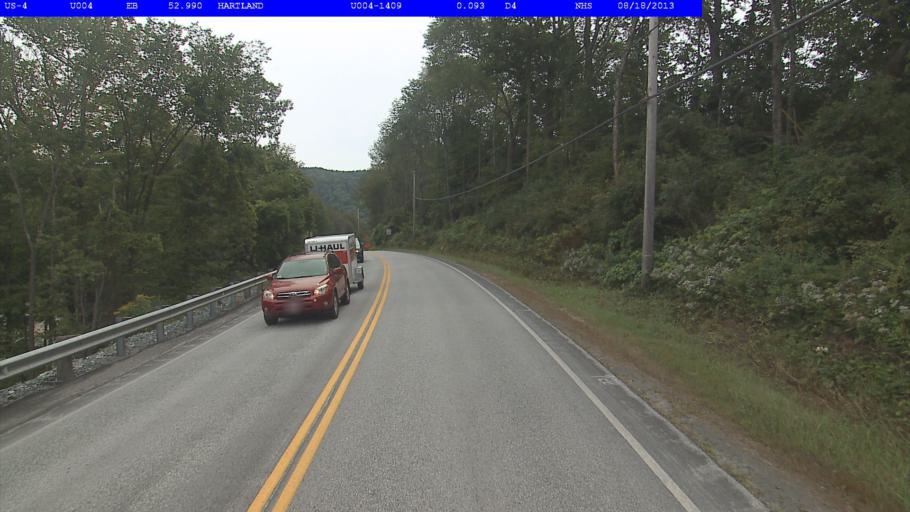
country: US
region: Vermont
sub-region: Windsor County
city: Woodstock
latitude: 43.6292
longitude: -72.4665
